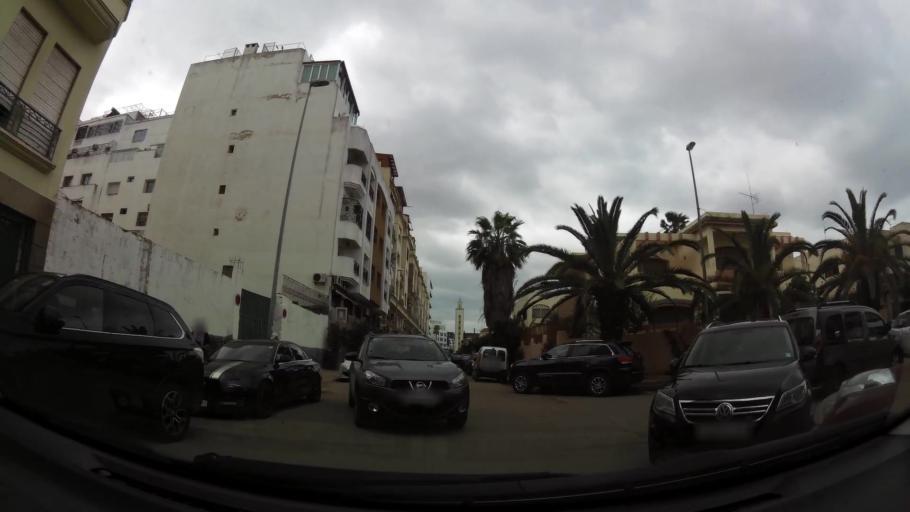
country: MA
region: Grand Casablanca
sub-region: Casablanca
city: Casablanca
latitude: 33.5695
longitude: -7.6541
